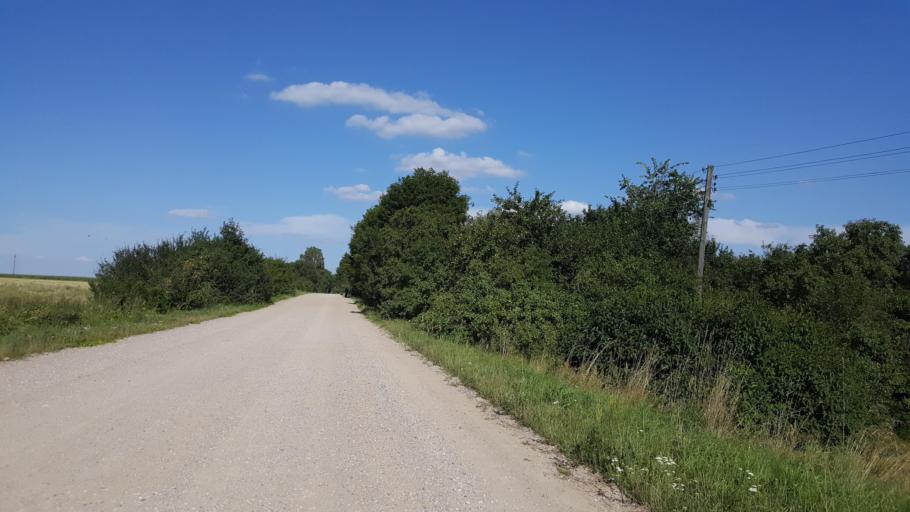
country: BY
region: Brest
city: Charnawchytsy
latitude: 52.3431
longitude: 23.6589
